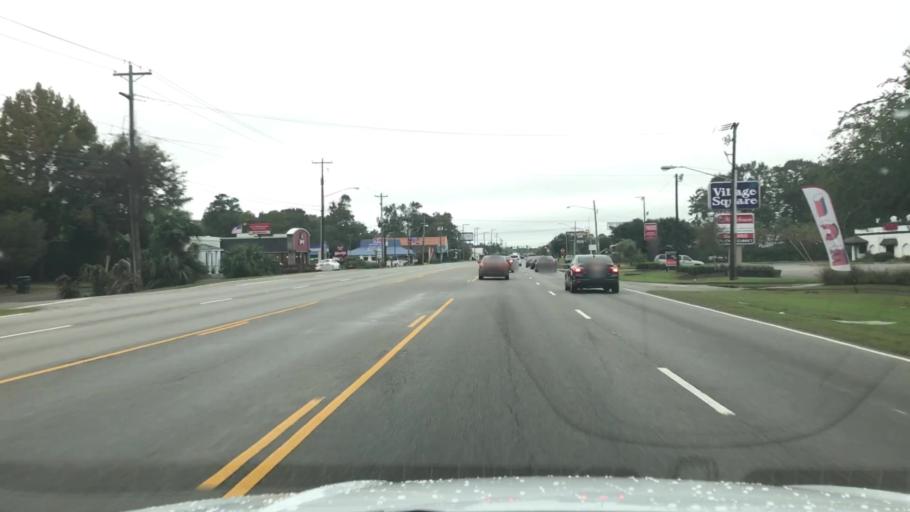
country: US
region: South Carolina
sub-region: Charleston County
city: North Charleston
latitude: 32.8045
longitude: -80.0129
